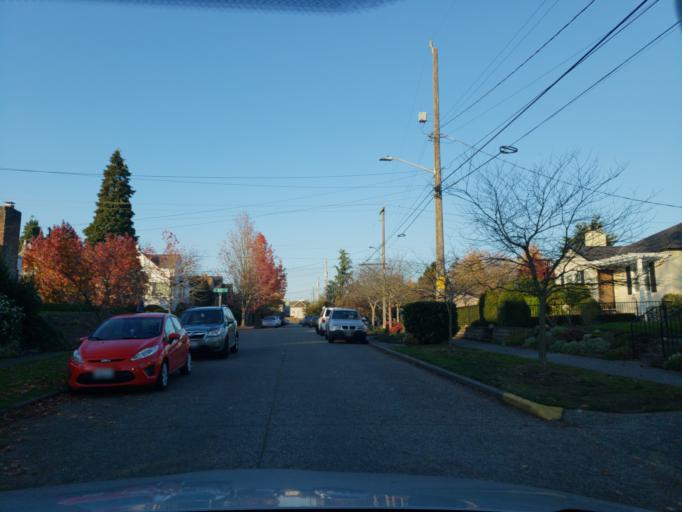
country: US
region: Washington
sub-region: King County
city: Shoreline
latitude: 47.6883
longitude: -122.3405
